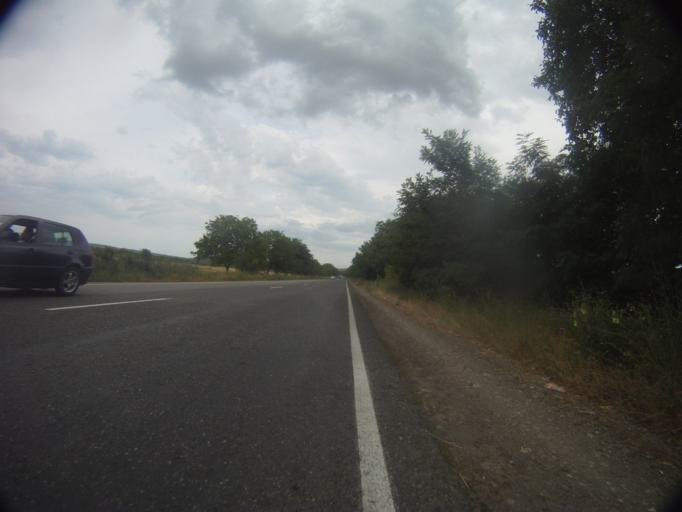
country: GE
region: Kakheti
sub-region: Gurjaani
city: Gurjaani
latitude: 41.6311
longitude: 45.7242
